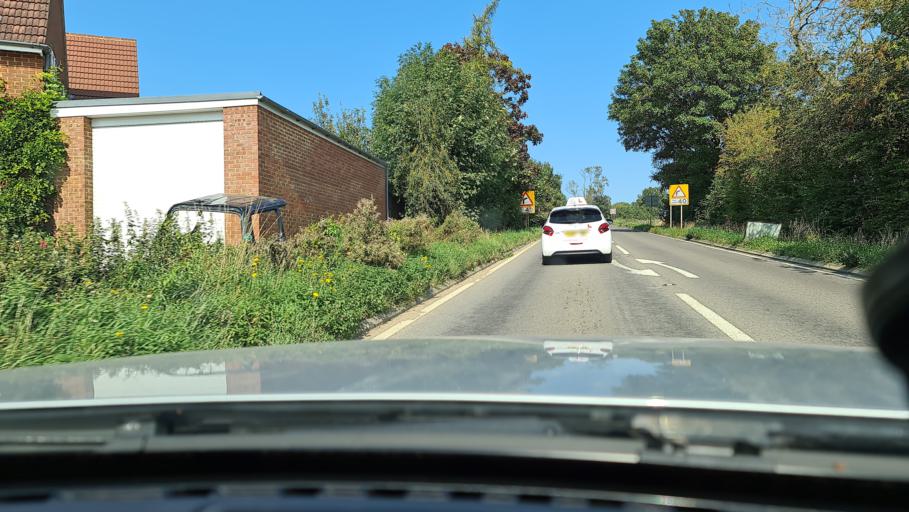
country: GB
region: England
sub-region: Northamptonshire
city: Daventry
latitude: 52.2830
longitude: -1.1689
